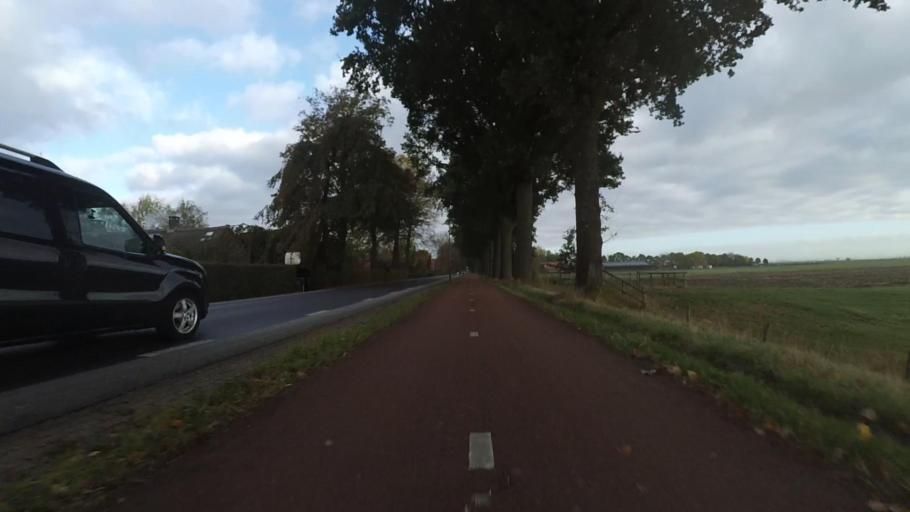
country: NL
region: North Holland
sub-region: Gemeente Blaricum
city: Blaricum
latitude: 52.2425
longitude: 5.2631
